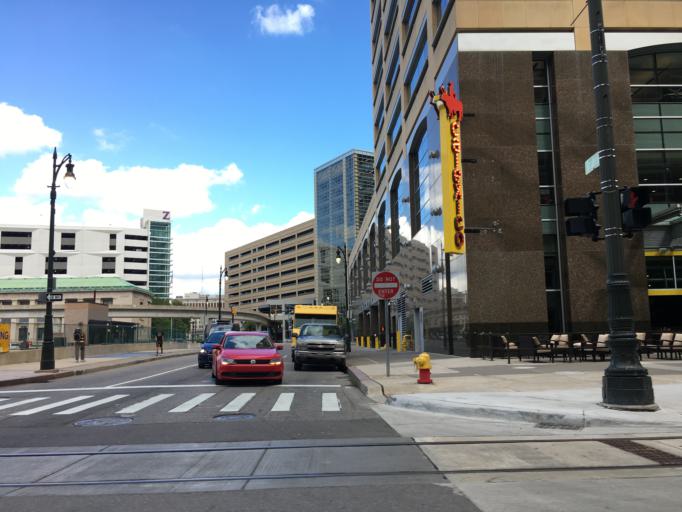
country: US
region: Michigan
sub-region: Wayne County
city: Detroit
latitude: 42.3328
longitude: -83.0474
